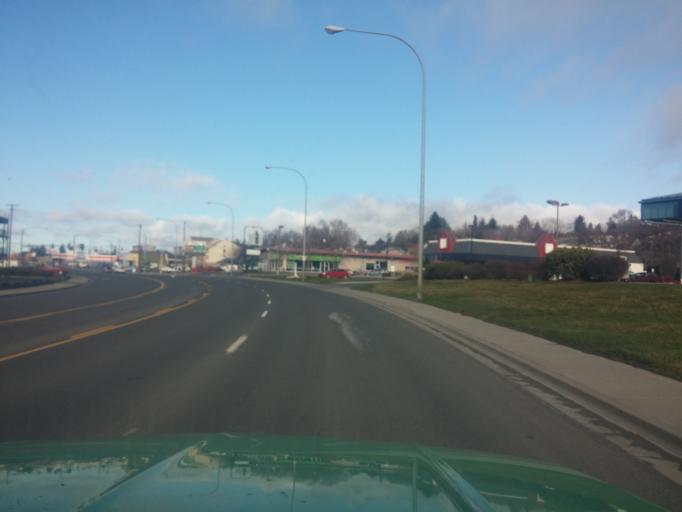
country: US
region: Idaho
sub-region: Latah County
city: Moscow
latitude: 46.7334
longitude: -117.0097
